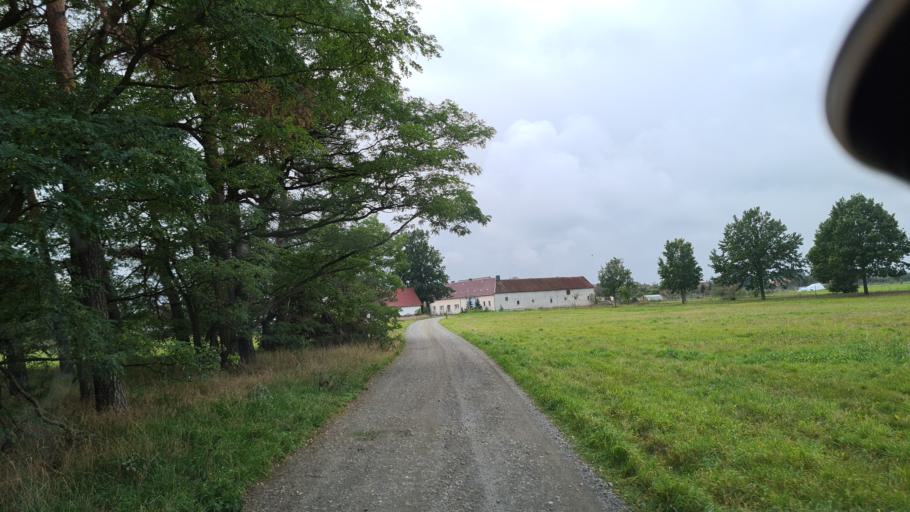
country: DE
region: Brandenburg
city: Schonewalde
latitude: 51.7019
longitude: 13.5735
